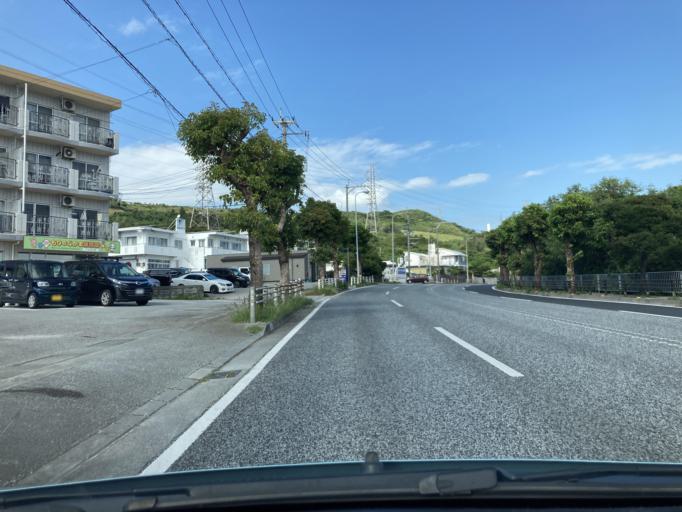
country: JP
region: Okinawa
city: Ginowan
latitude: 26.2701
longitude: 127.7915
